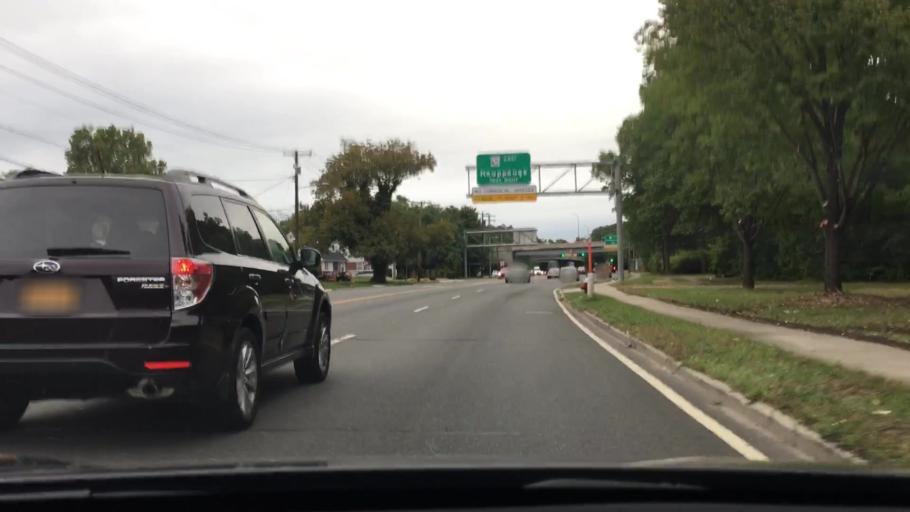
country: US
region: New York
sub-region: Nassau County
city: Carle Place
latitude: 40.7527
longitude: -73.6186
